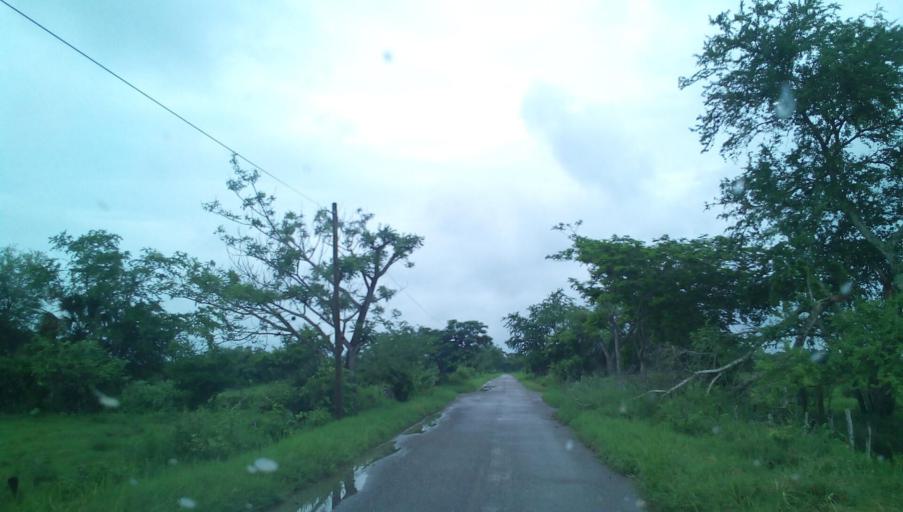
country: MX
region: Veracruz
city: Tempoal de Sanchez
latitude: 21.4783
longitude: -98.4192
